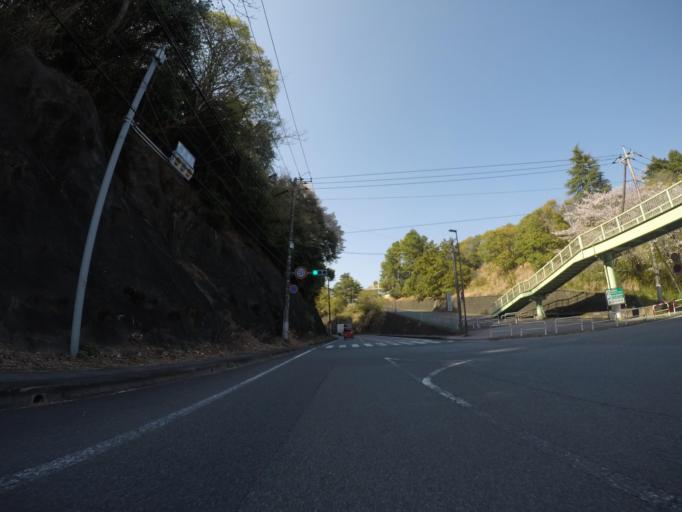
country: JP
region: Shizuoka
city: Mishima
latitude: 35.0411
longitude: 138.9232
